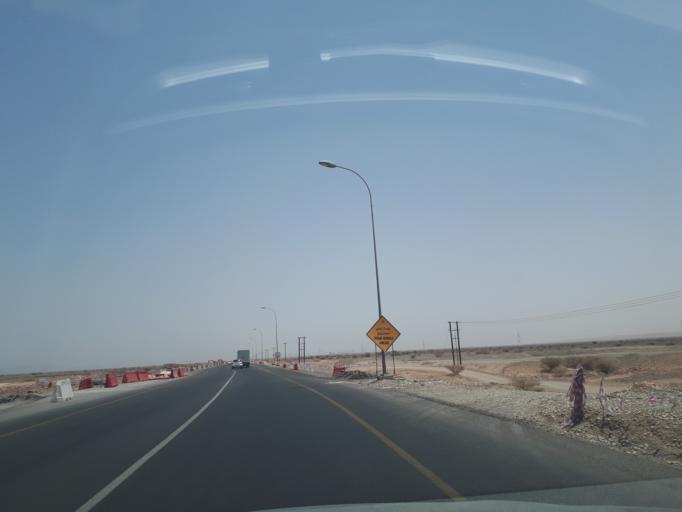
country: OM
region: Ash Sharqiyah
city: Badiyah
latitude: 22.4299
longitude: 59.0350
